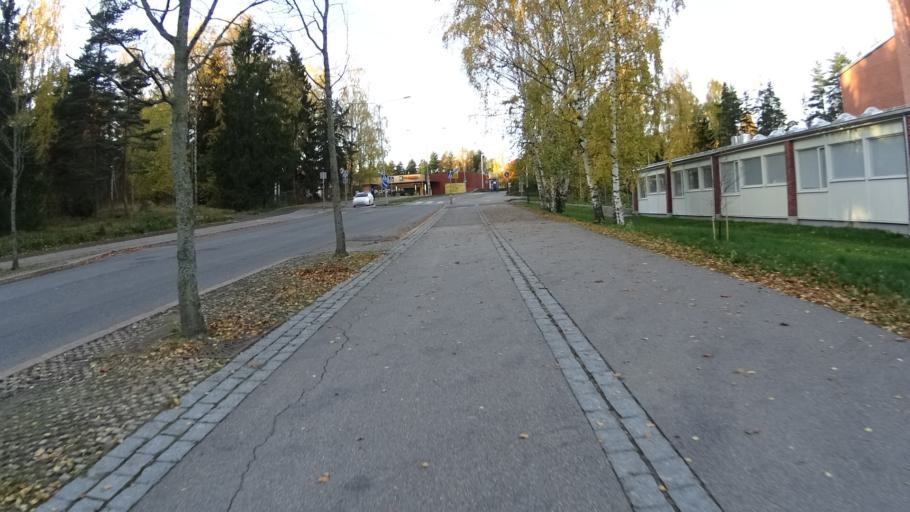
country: FI
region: Uusimaa
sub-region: Helsinki
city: Helsinki
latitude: 60.2315
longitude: 24.9601
